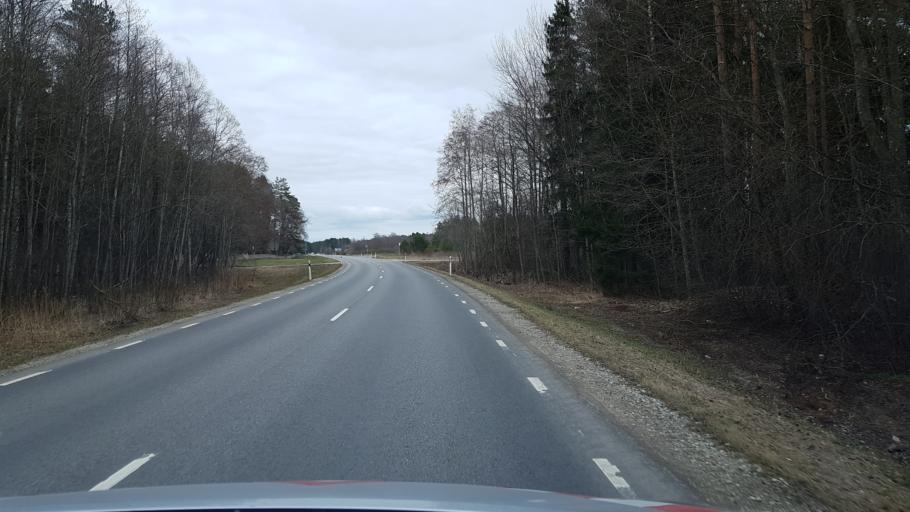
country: EE
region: Ida-Virumaa
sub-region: Narva-Joesuu linn
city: Narva-Joesuu
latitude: 59.4137
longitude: 28.0860
